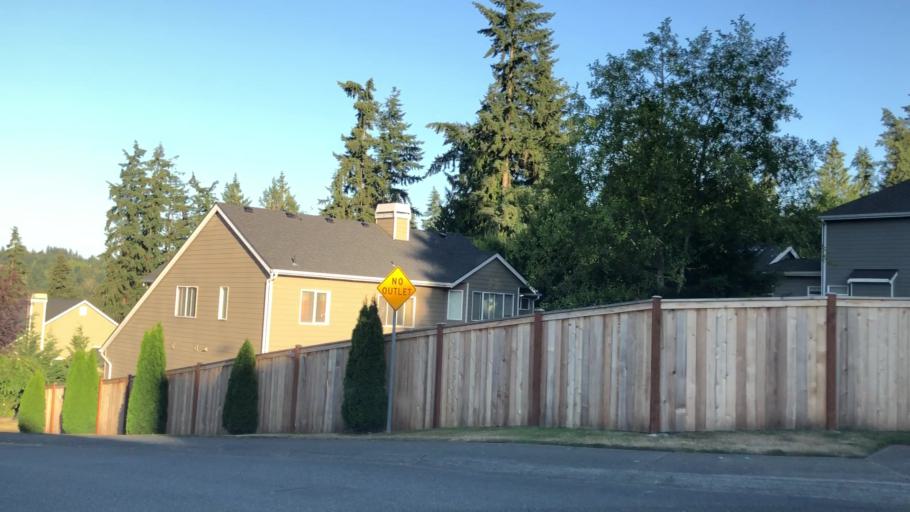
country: US
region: Washington
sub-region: King County
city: Redmond
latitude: 47.6901
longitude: -122.0957
